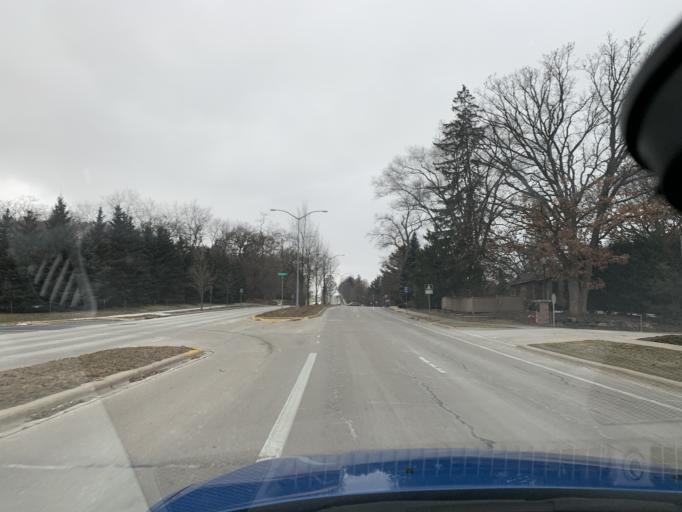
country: US
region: Wisconsin
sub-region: Dane County
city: Middleton
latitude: 43.0749
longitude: -89.5306
